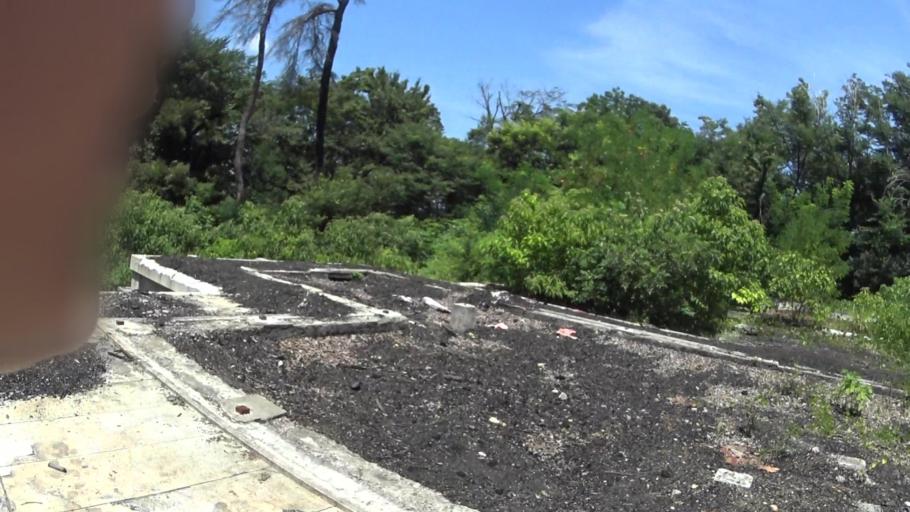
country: JP
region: Gunma
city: Ota
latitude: 36.3007
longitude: 139.3734
